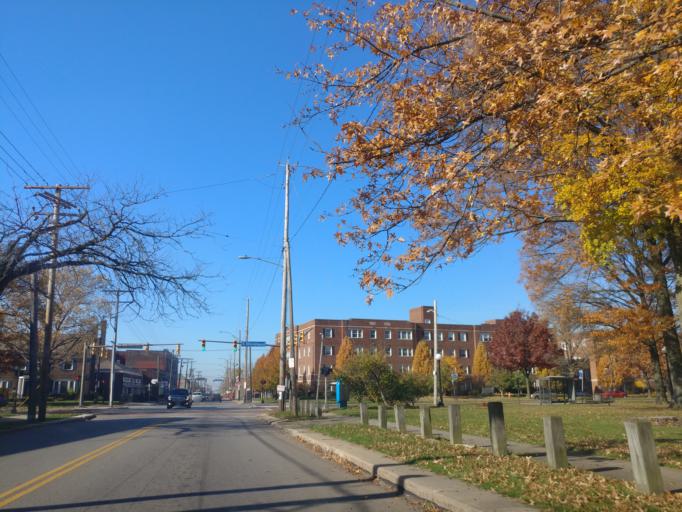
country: US
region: Ohio
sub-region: Cuyahoga County
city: Cleveland Heights
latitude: 41.4796
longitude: -81.5898
